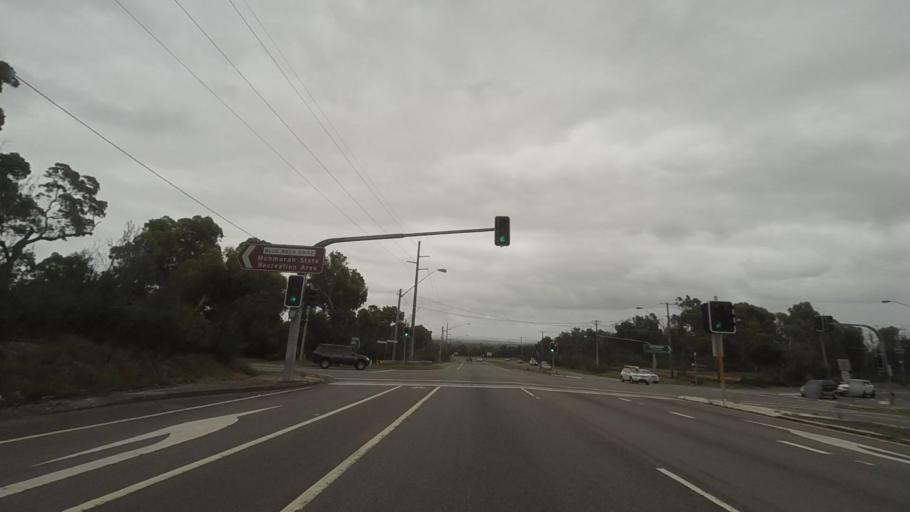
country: AU
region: New South Wales
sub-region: Wyong Shire
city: Kingfisher Shores
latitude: -33.1813
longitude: 151.5952
